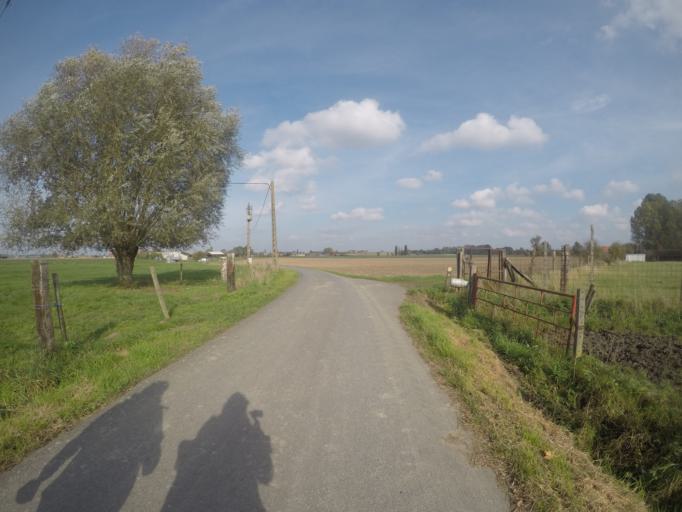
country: BE
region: Flanders
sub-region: Provincie West-Vlaanderen
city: Moorslede
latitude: 50.8500
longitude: 3.0631
